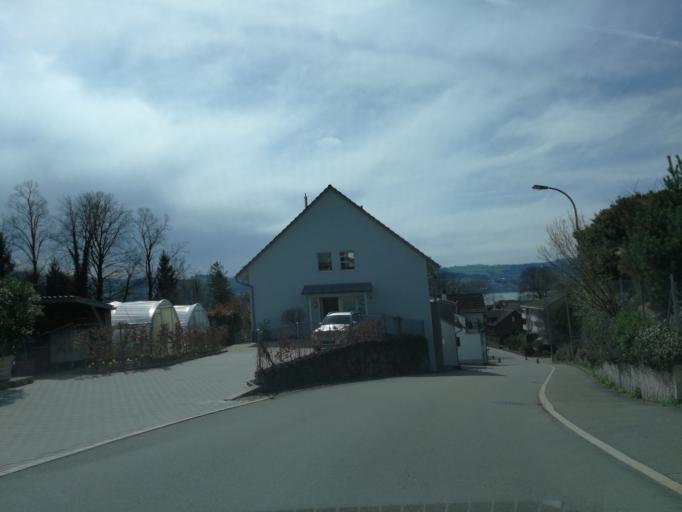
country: CH
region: Zurich
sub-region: Bezirk Meilen
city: Maennedorf / Dorfkern
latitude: 47.2558
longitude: 8.6945
